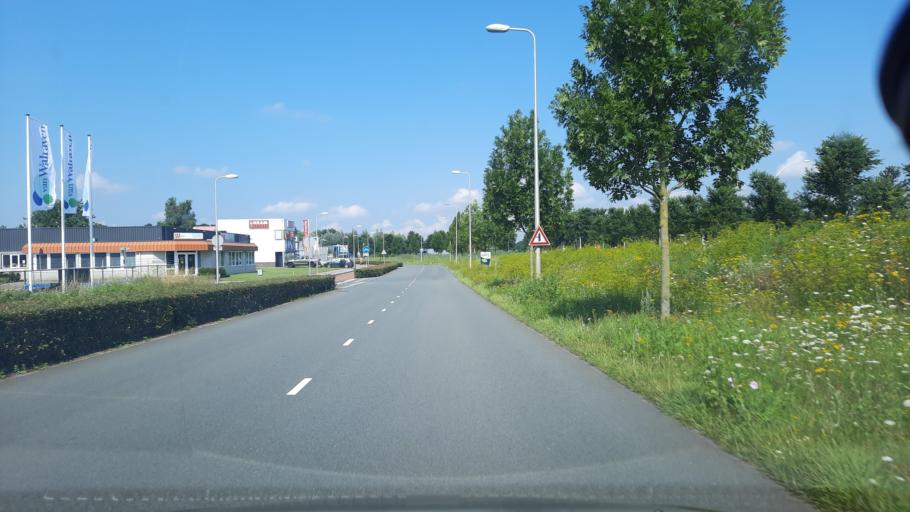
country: NL
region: Gelderland
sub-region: Gemeente Hattem
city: Hattem
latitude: 52.5112
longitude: 6.0522
